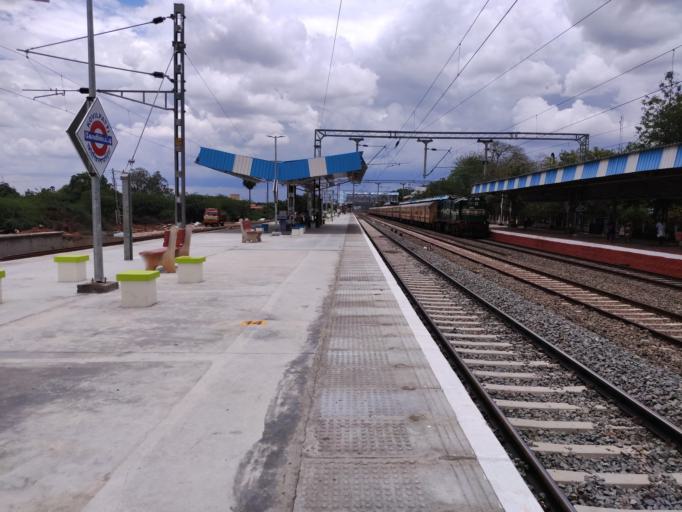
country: IN
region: Tamil Nadu
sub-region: Thoothukkudi
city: Kovilpatti
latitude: 9.1815
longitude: 77.8713
